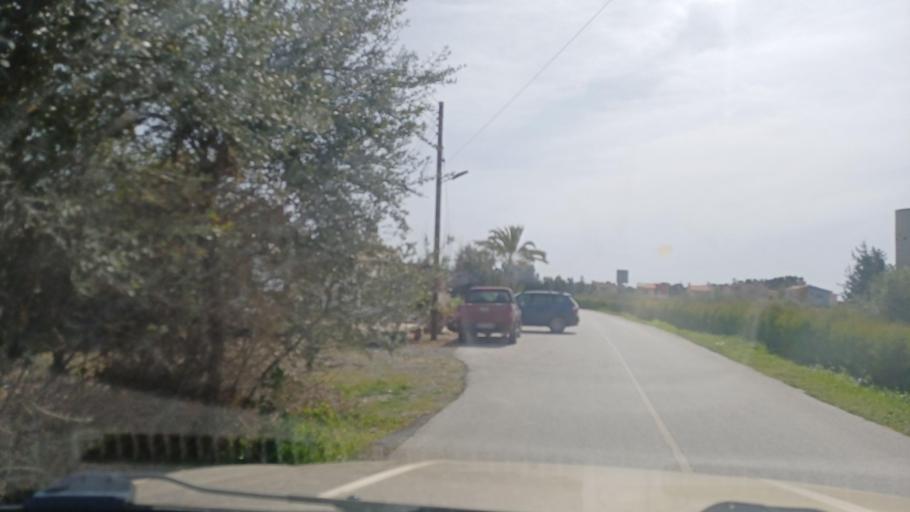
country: CY
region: Pafos
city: Paphos
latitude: 34.7538
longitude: 32.4677
